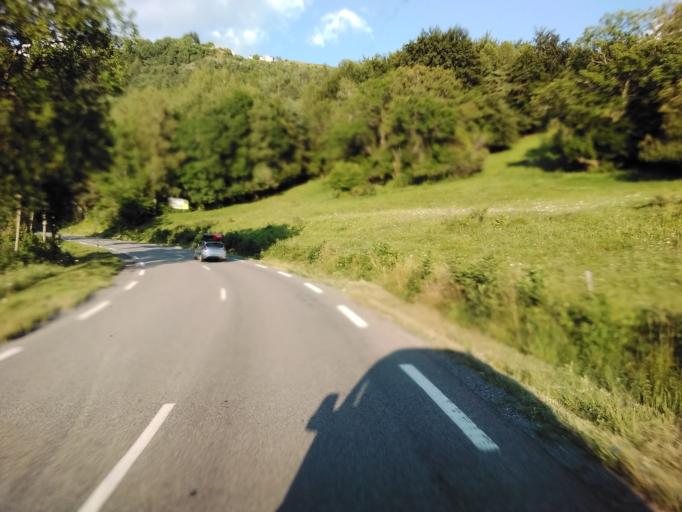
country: FR
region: Provence-Alpes-Cote d'Azur
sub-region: Departement des Alpes-de-Haute-Provence
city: Seyne-les-Alpes
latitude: 44.4437
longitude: 6.3655
